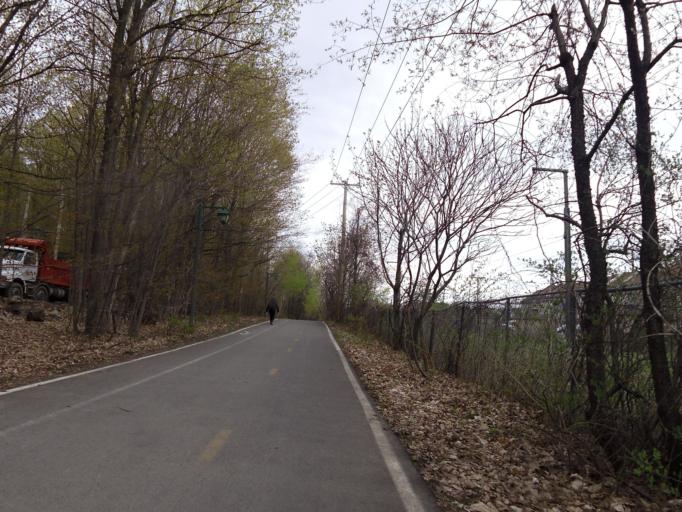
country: CA
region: Quebec
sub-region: Laurentides
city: Deux-Montagnes
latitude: 45.5436
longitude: -73.9073
